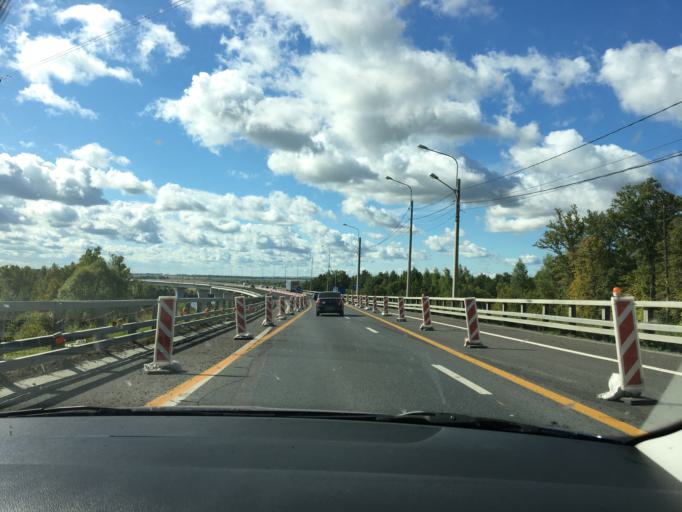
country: RU
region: Chuvashia
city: Yadrin
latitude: 56.0363
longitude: 46.2479
